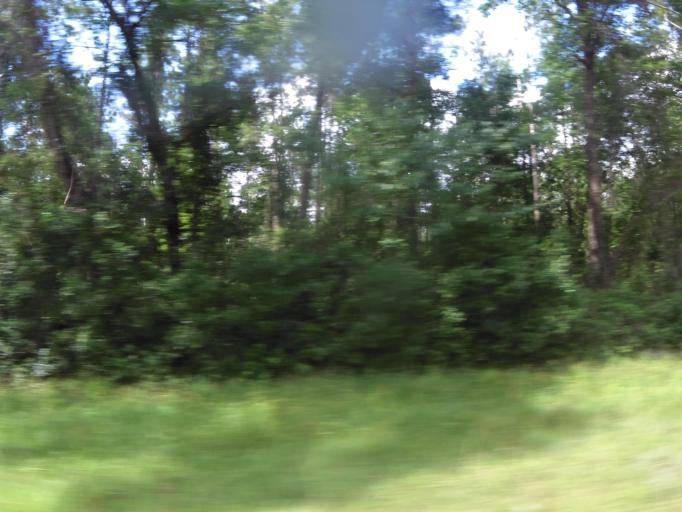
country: US
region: Florida
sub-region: Baker County
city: Macclenny
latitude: 30.2605
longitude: -82.0992
